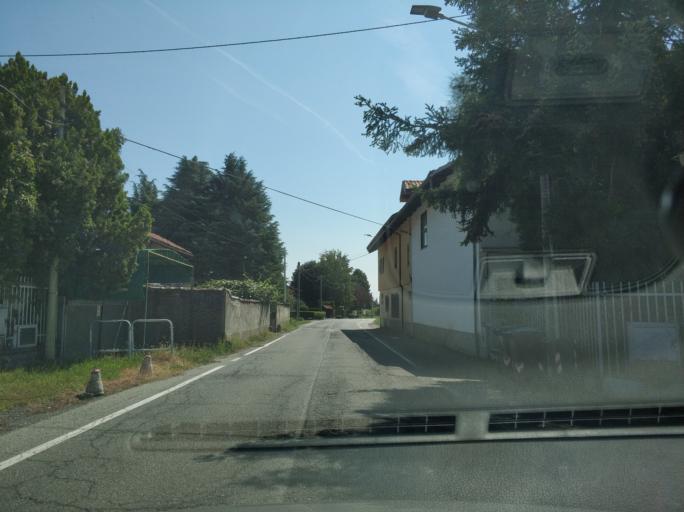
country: IT
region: Piedmont
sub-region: Provincia di Torino
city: San Maurizio
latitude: 45.2354
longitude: 7.6366
